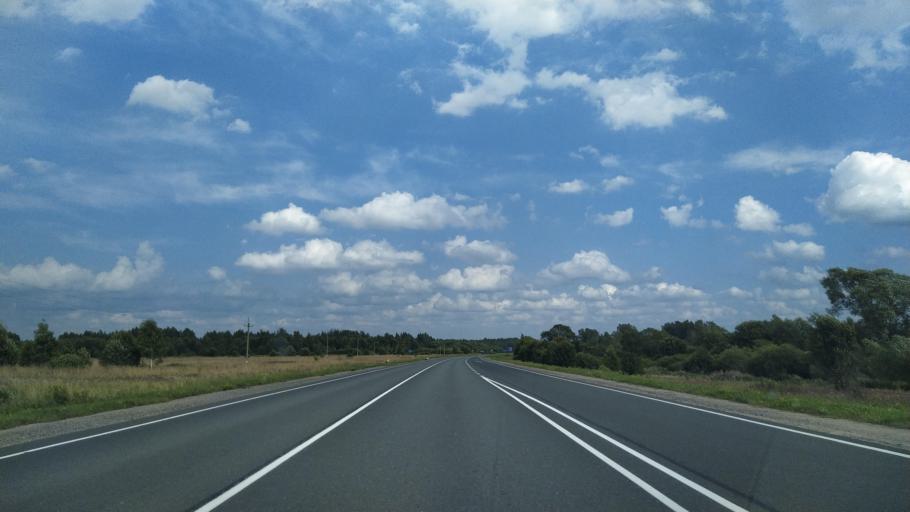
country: RU
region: Pskov
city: Dno
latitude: 57.9832
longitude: 29.7588
